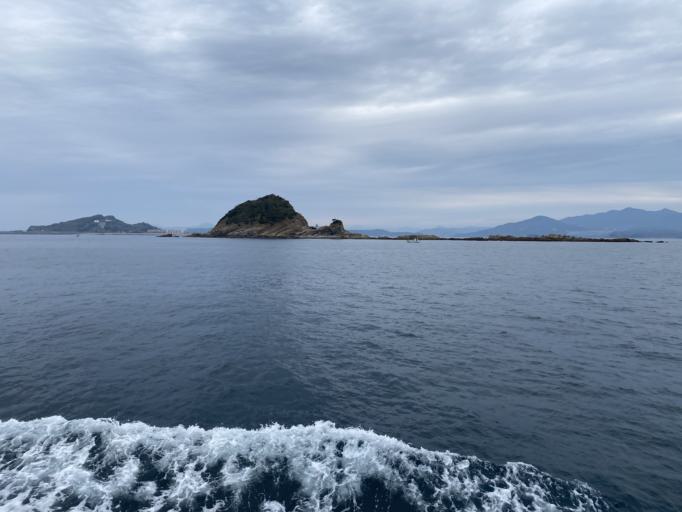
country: JP
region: Nagasaki
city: Nagasaki-shi
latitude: 32.6299
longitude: 129.7430
